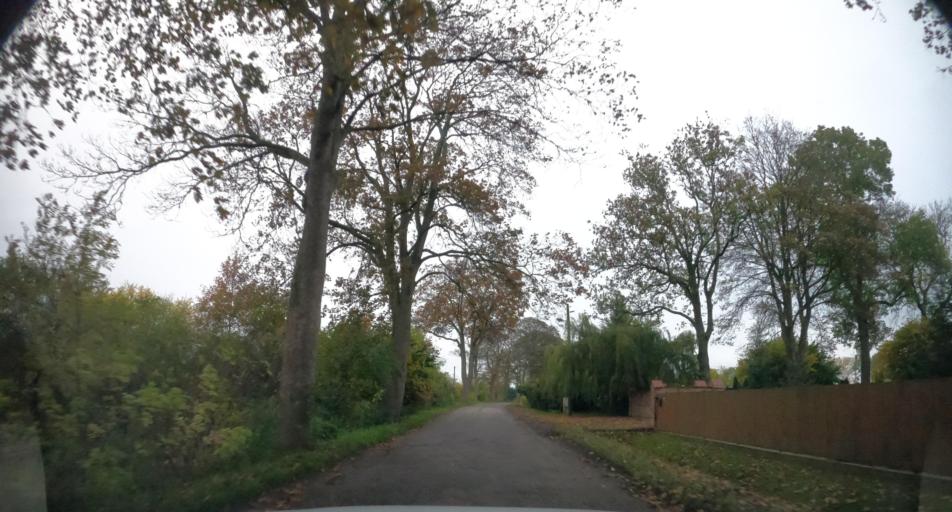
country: PL
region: West Pomeranian Voivodeship
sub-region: Powiat kamienski
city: Wolin
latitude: 53.9081
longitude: 14.6184
